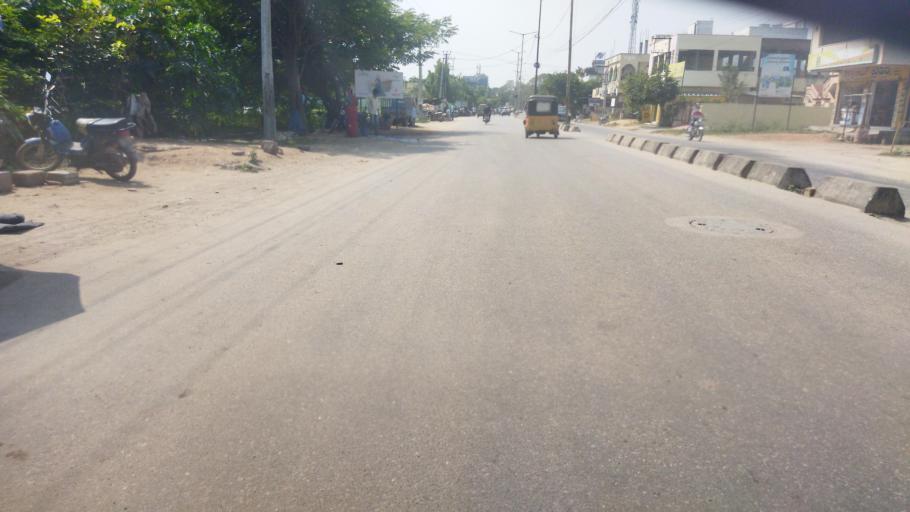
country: IN
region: Telangana
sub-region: Nalgonda
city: Nalgonda
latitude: 17.0725
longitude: 79.2849
